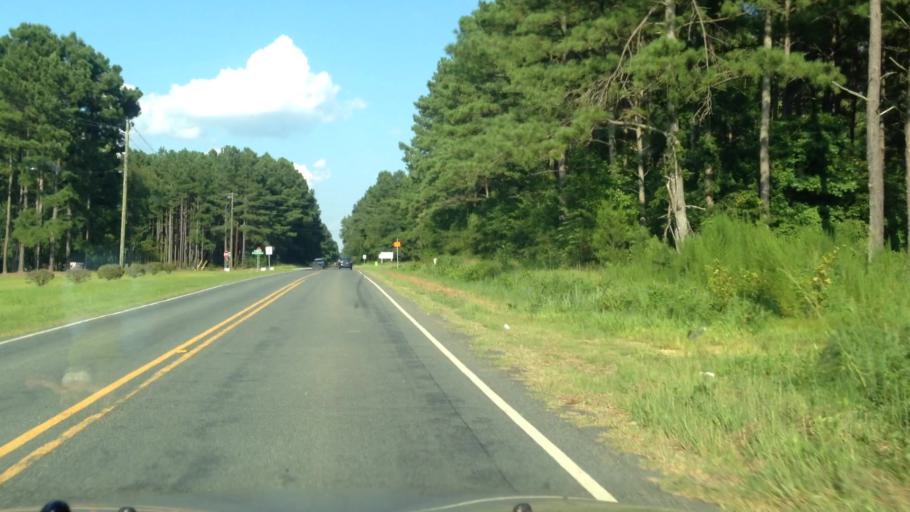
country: US
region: North Carolina
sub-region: Harnett County
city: Buies Creek
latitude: 35.4104
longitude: -78.7262
